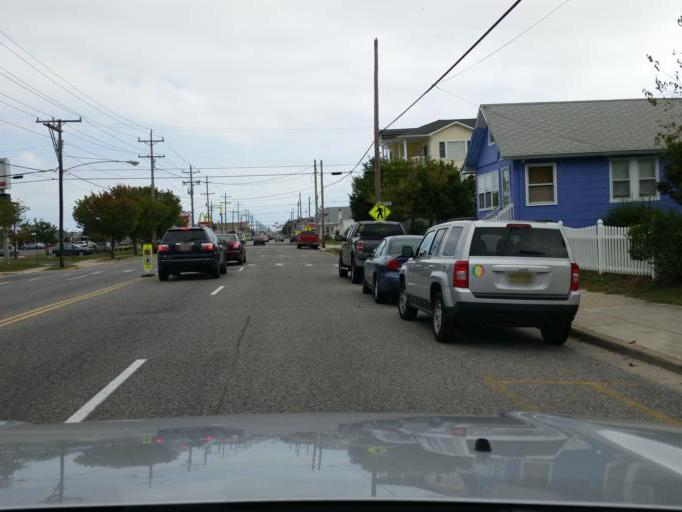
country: US
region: New Jersey
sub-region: Cape May County
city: Wildwood Crest
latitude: 38.9842
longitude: -74.8293
